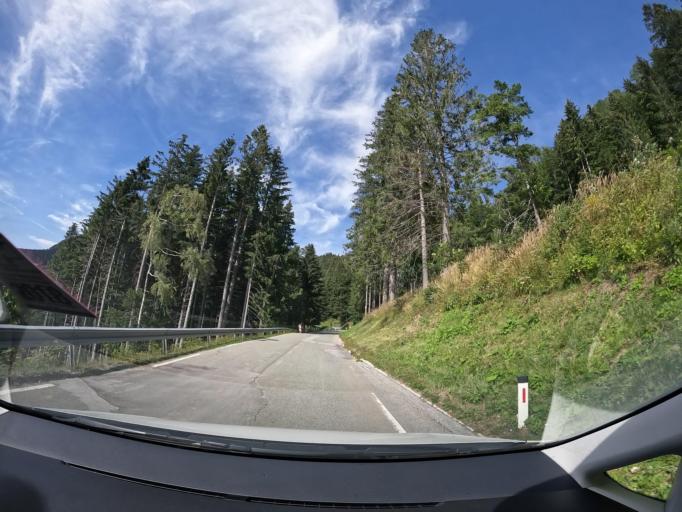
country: AT
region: Carinthia
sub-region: Politischer Bezirk Klagenfurt Land
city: Maria Saal
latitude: 46.6960
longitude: 14.3160
